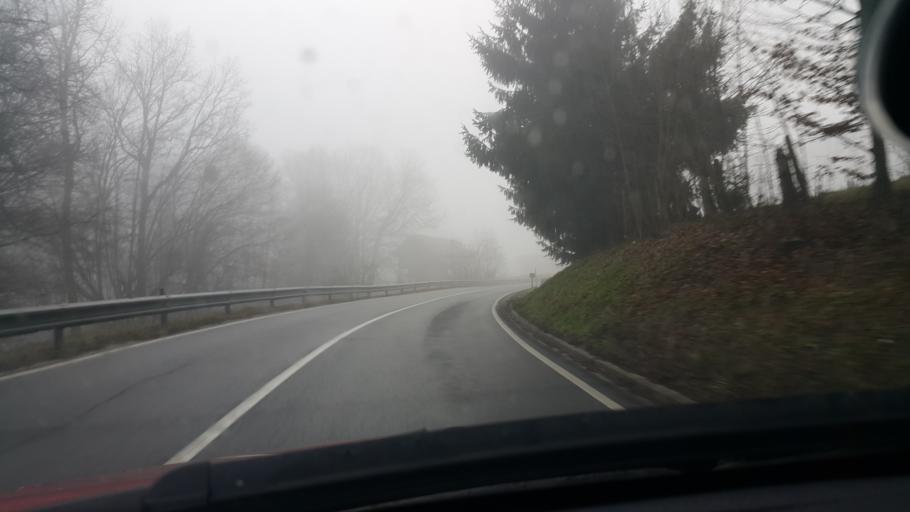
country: SI
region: Podcetrtek
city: Podcetrtek
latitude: 46.1133
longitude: 15.6017
